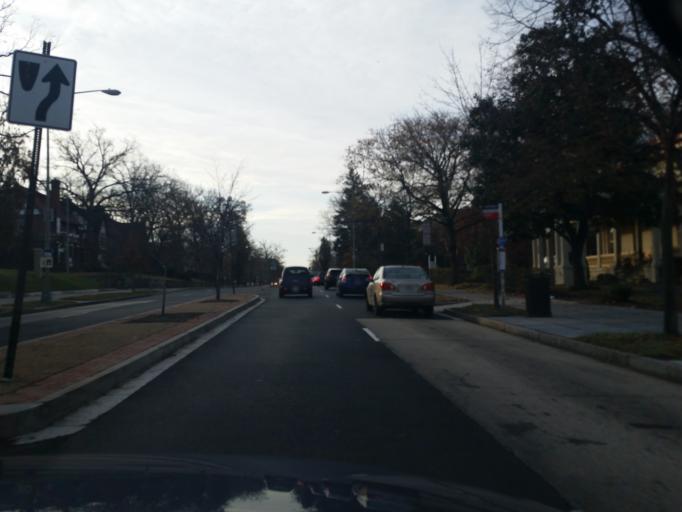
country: US
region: Maryland
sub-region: Montgomery County
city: Takoma Park
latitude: 38.9504
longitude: -77.0364
